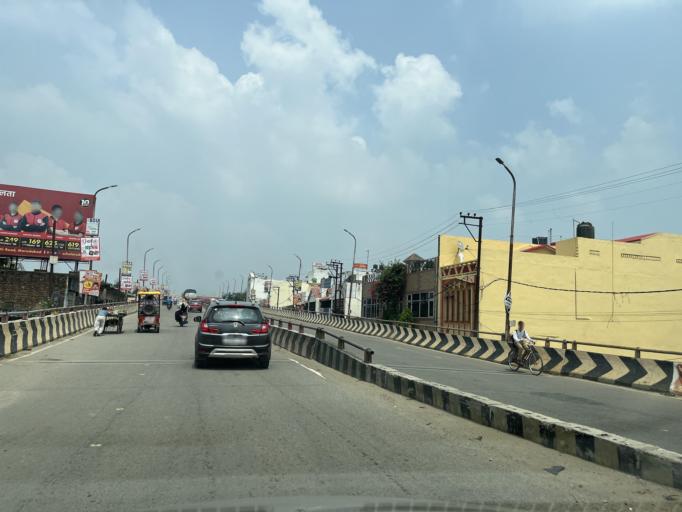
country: IN
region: Uttar Pradesh
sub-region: Bijnor
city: Najibabad
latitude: 29.6032
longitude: 78.3438
